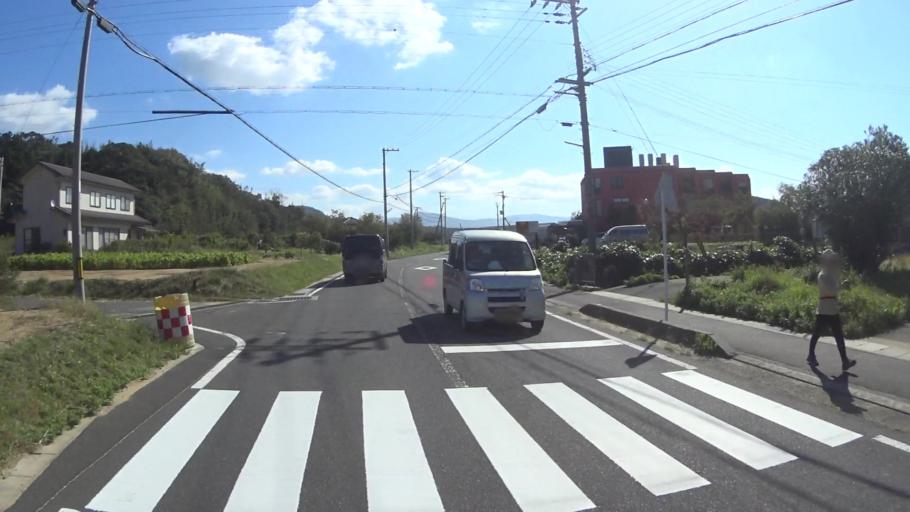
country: JP
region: Kyoto
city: Miyazu
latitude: 35.6941
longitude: 135.0416
